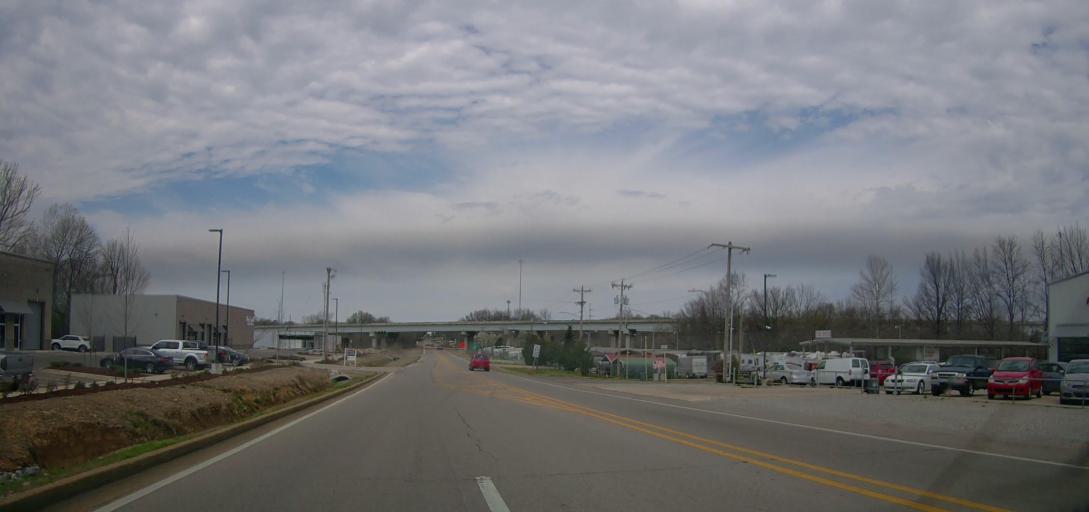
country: US
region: Mississippi
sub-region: De Soto County
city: Olive Branch
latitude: 34.9663
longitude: -89.8312
